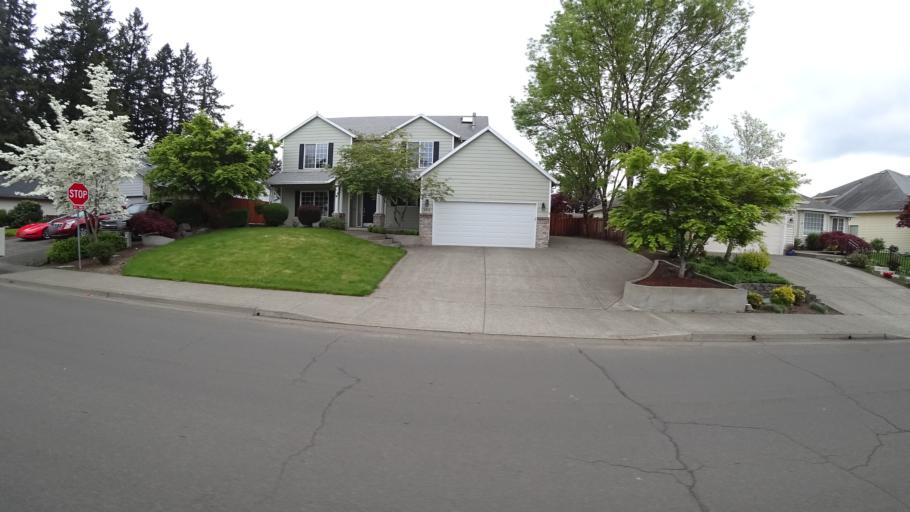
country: US
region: Oregon
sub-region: Washington County
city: Hillsboro
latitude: 45.5442
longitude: -122.9829
